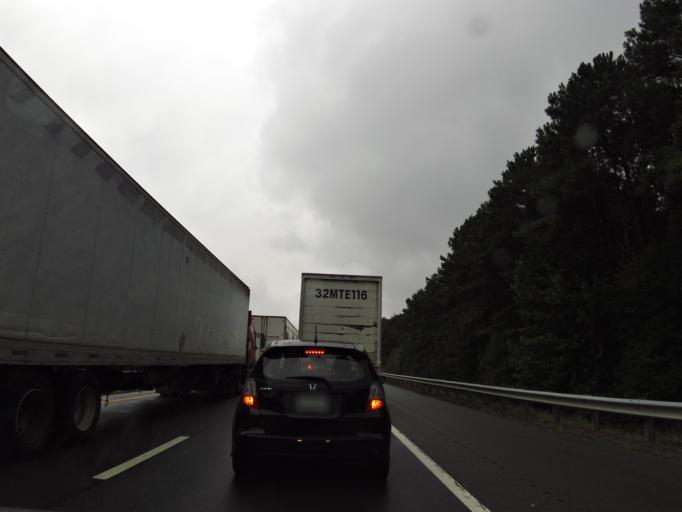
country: US
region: Tennessee
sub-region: Bradley County
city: Hopewell
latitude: 35.2254
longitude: -84.8580
